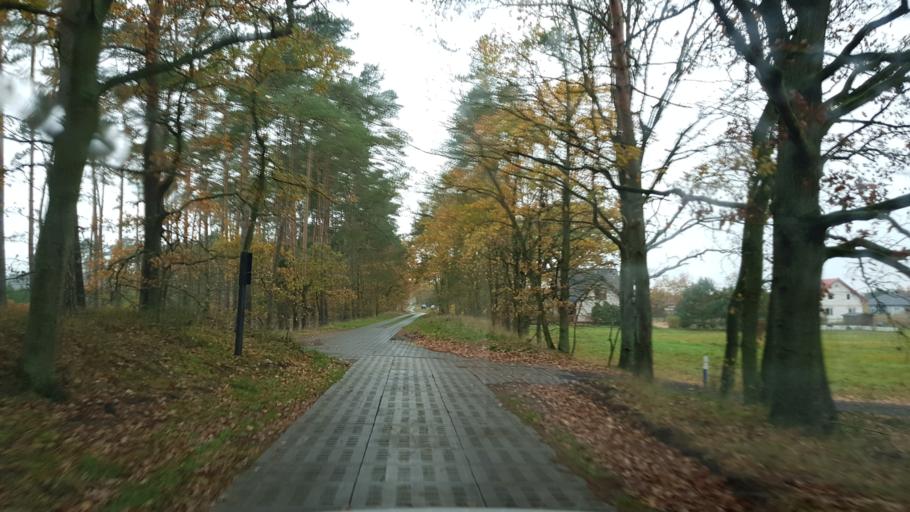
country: PL
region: West Pomeranian Voivodeship
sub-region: Powiat goleniowski
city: Goleniow
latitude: 53.5800
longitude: 14.7835
